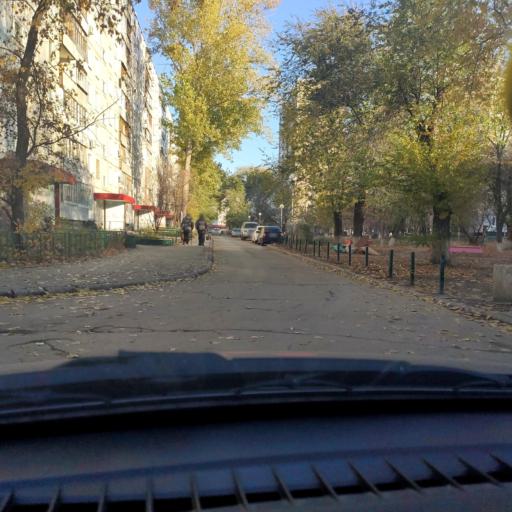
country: RU
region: Samara
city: Tol'yatti
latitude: 53.5125
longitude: 49.2799
